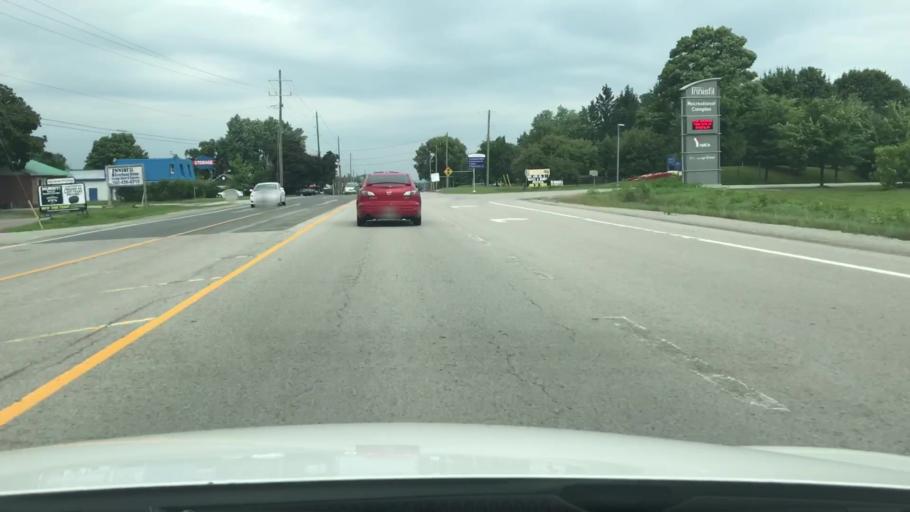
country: CA
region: Ontario
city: Innisfil
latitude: 44.2971
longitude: -79.6127
